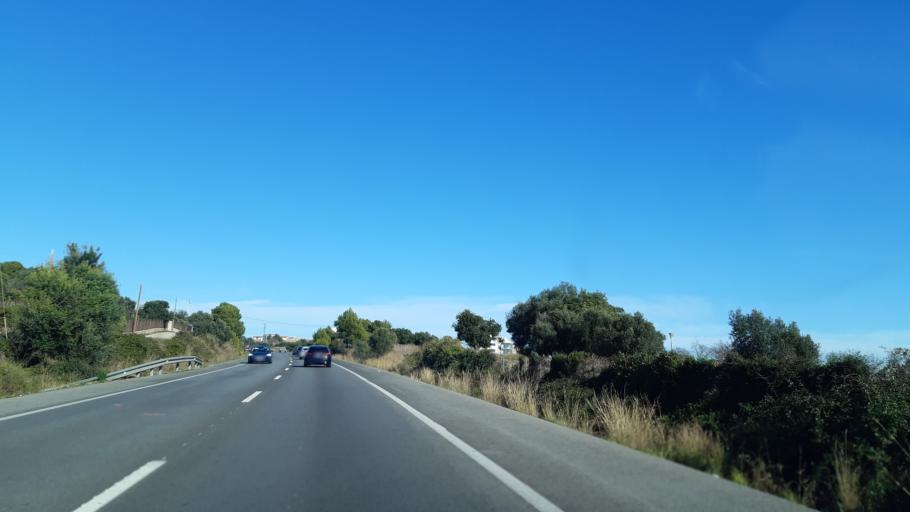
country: ES
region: Catalonia
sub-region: Provincia de Barcelona
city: Vilanova i la Geltru
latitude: 41.2177
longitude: 1.6986
